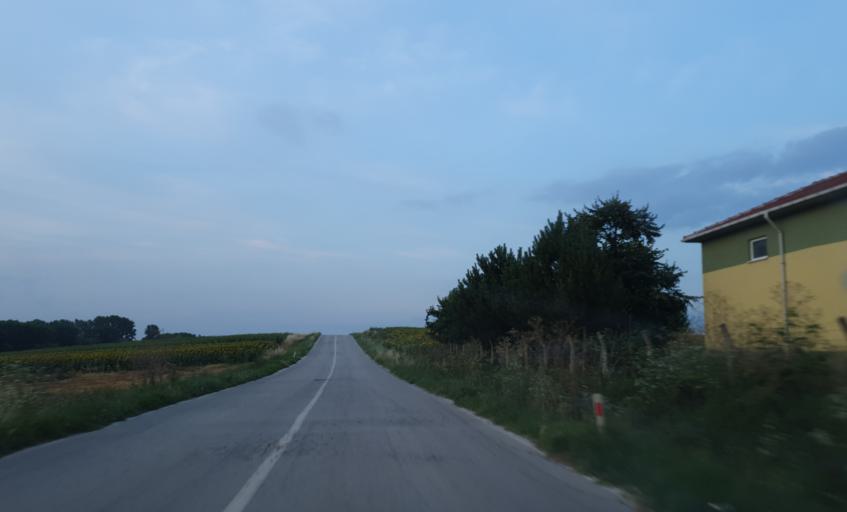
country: TR
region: Tekirdag
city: Beyazkoy
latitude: 41.3958
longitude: 27.6331
